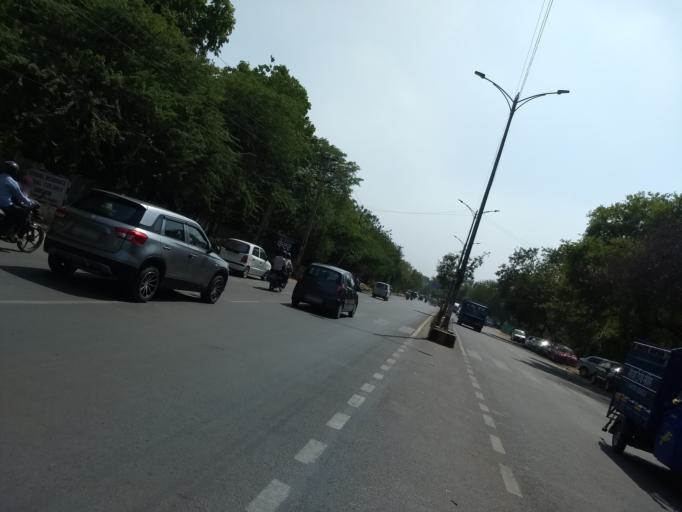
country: IN
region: Haryana
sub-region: Gurgaon
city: Gurgaon
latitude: 28.4709
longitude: 77.0486
